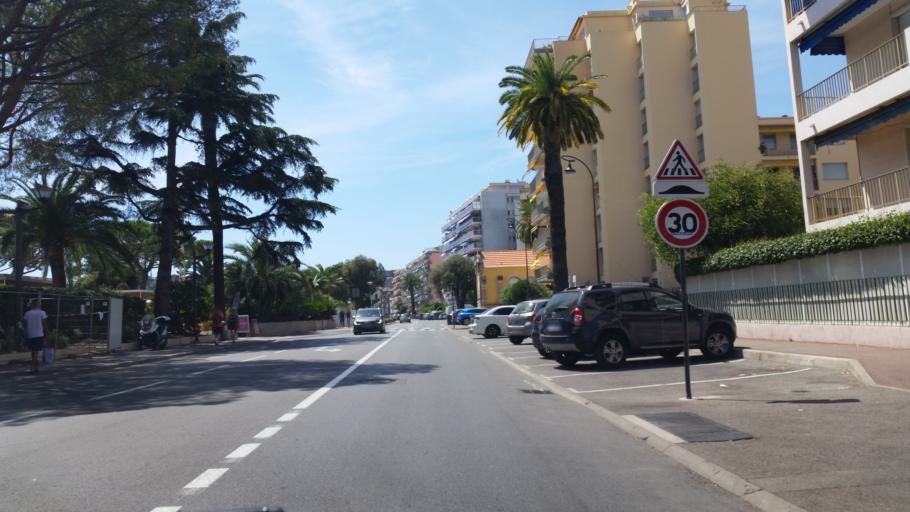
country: FR
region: Provence-Alpes-Cote d'Azur
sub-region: Departement des Alpes-Maritimes
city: Roquebrune-Cap-Martin
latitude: 43.7650
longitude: 7.4875
